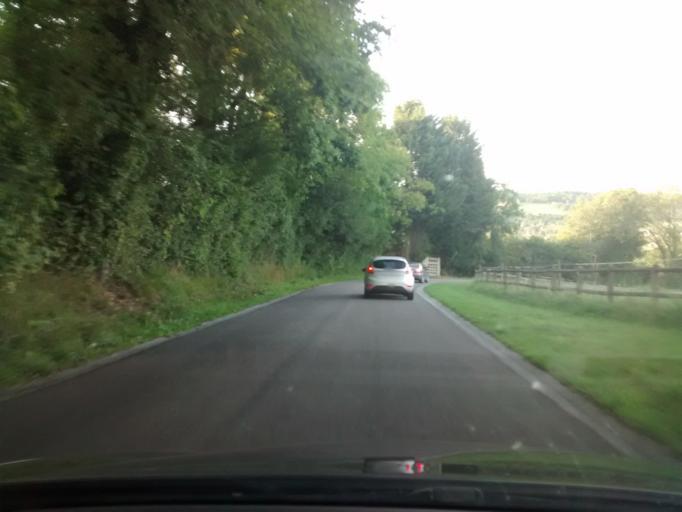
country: FR
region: Lower Normandy
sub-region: Departement du Calvados
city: Blonville-sur-Mer
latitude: 49.3237
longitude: 0.0276
